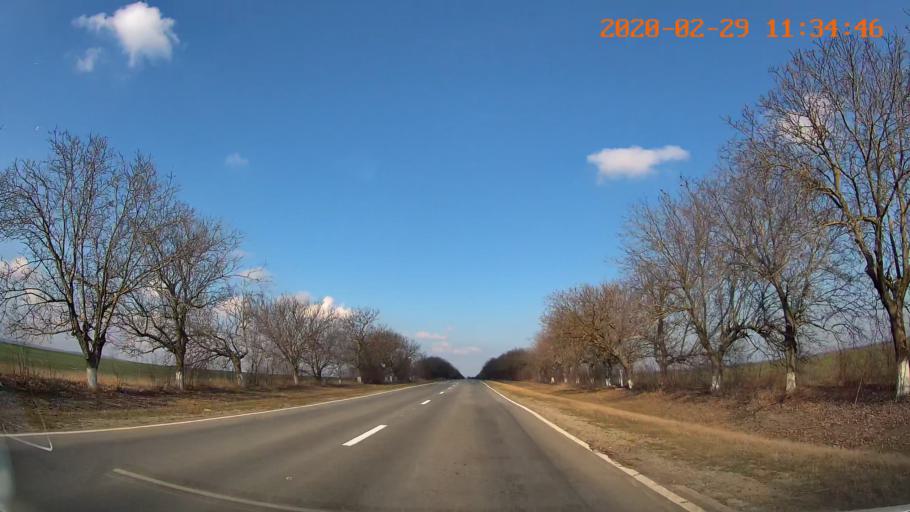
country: MD
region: Rezina
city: Saharna
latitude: 47.5705
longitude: 29.0702
